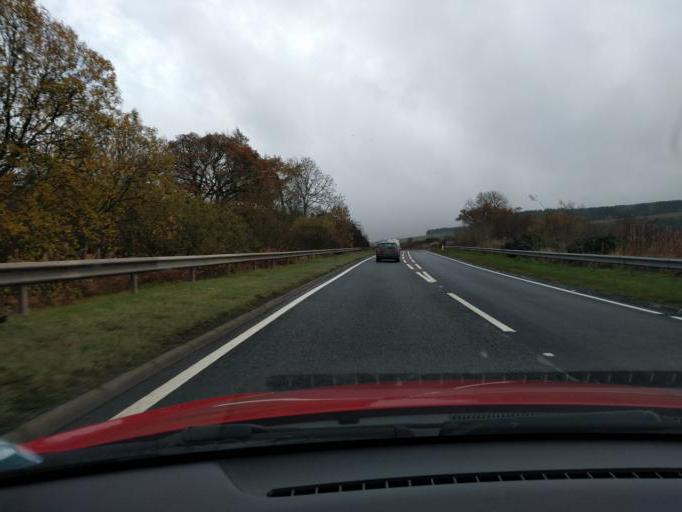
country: GB
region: Scotland
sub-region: The Scottish Borders
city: Chirnside
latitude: 55.8773
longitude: -2.2835
